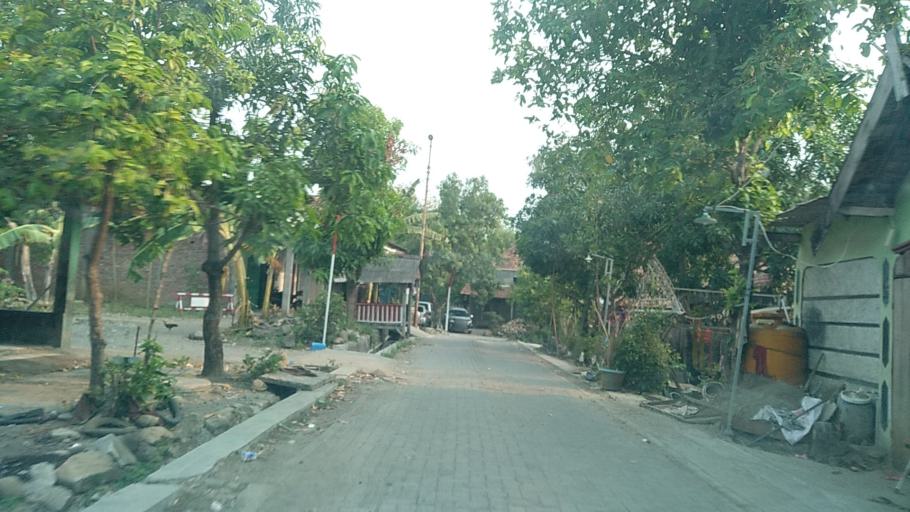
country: ID
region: Central Java
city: Mranggen
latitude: -7.0685
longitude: 110.4839
